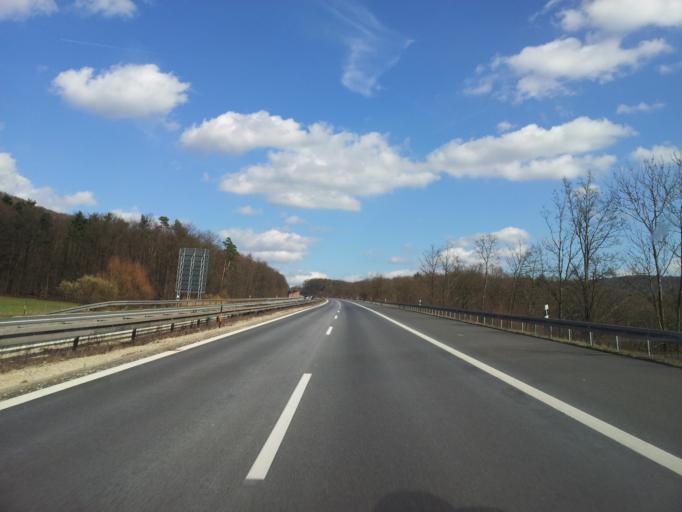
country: DE
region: Bavaria
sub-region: Upper Franconia
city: Schesslitz
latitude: 49.9822
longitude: 11.0540
